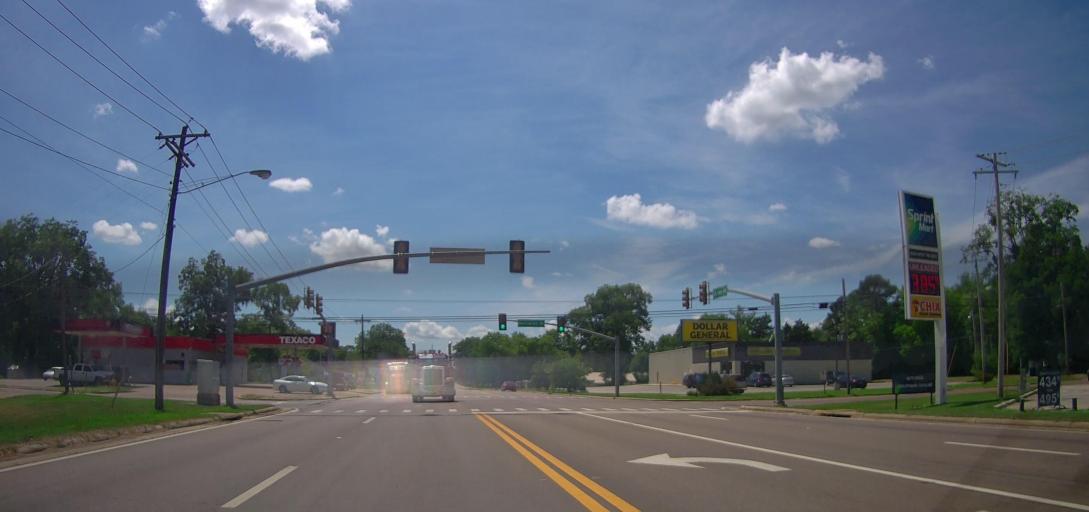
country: US
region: Mississippi
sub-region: Monroe County
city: Aberdeen
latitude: 33.8153
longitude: -88.5435
